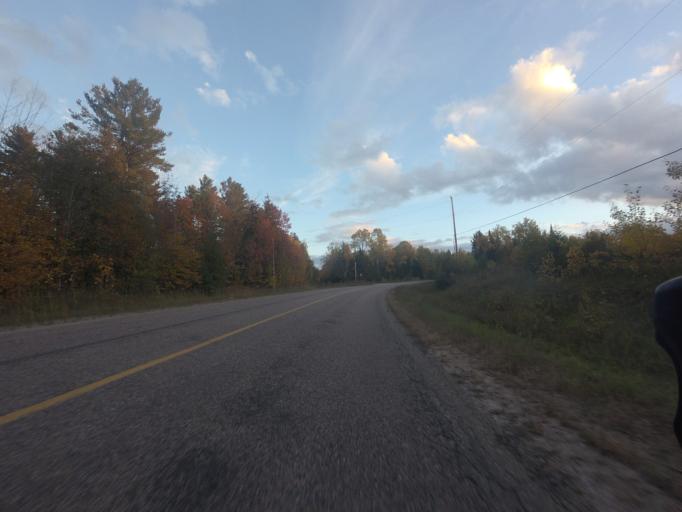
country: CA
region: Ontario
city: Renfrew
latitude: 45.4186
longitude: -76.9521
